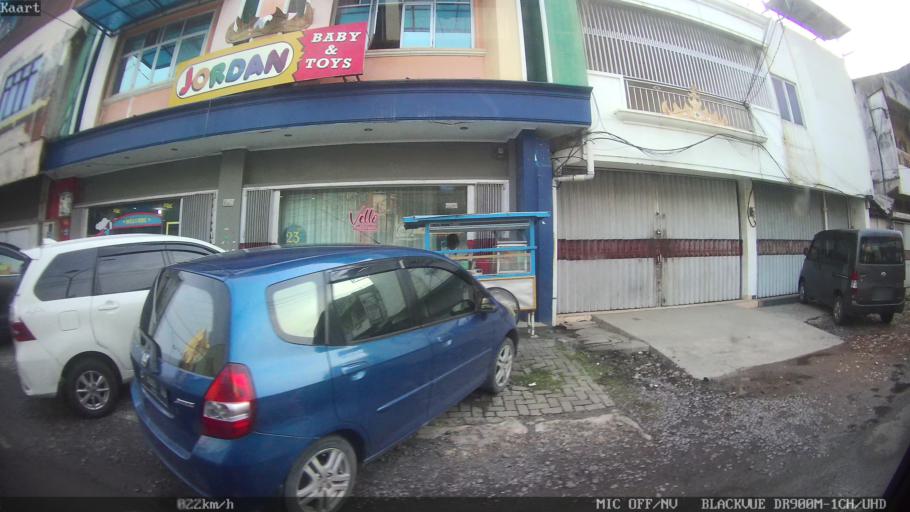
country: ID
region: Lampung
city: Bandarlampung
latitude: -5.4483
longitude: 105.2657
